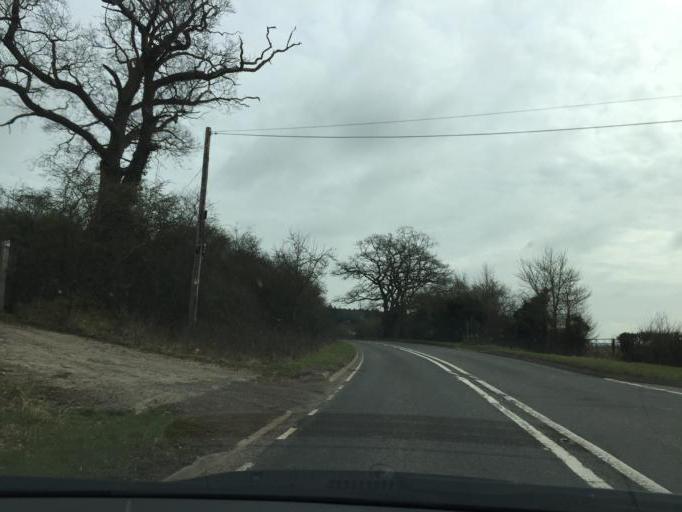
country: GB
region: England
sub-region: Warwickshire
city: Studley
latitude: 52.2989
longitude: -1.8675
